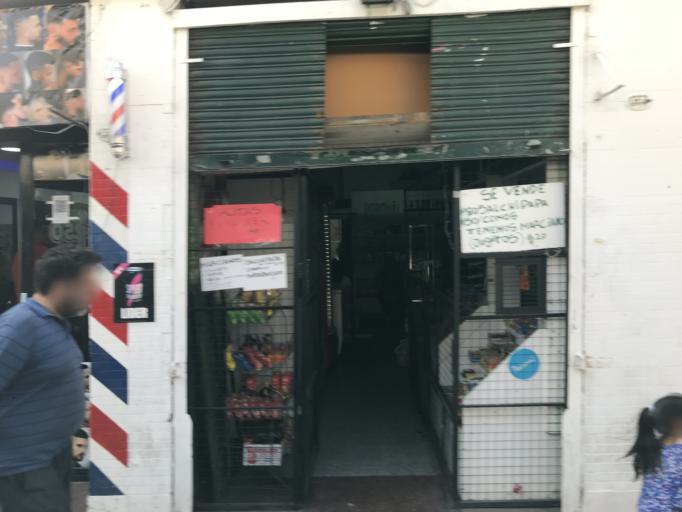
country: AR
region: Buenos Aires F.D.
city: Buenos Aires
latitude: -34.6283
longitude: -58.3852
